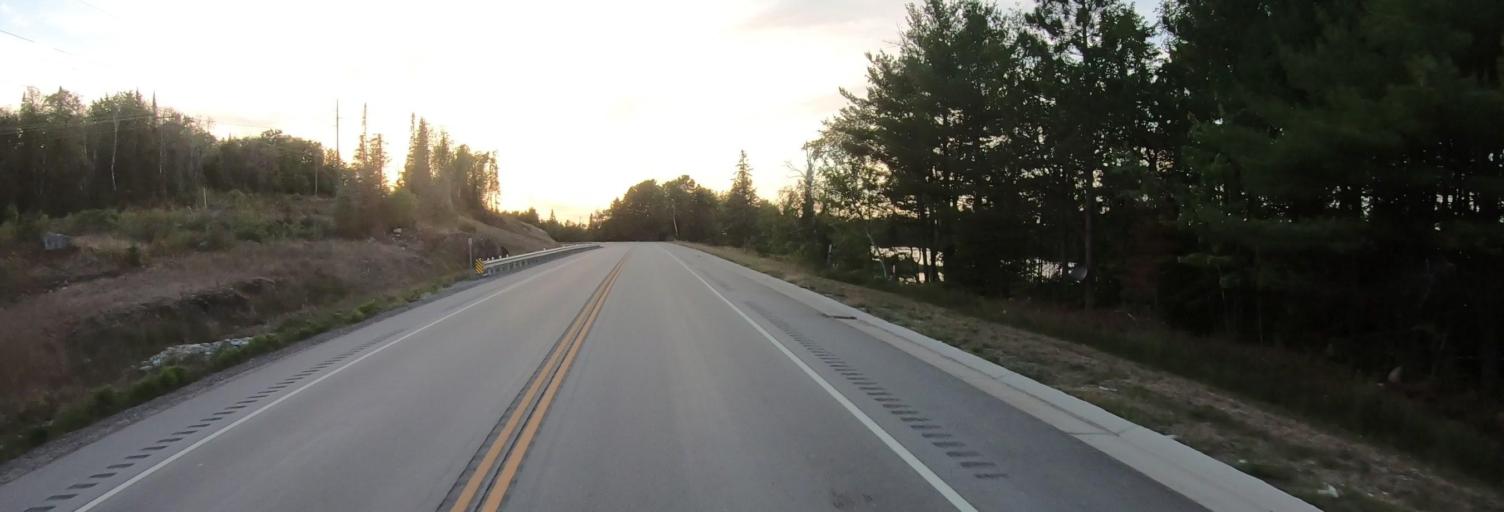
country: US
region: Minnesota
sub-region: Saint Louis County
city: Babbitt
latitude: 47.8555
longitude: -92.0636
